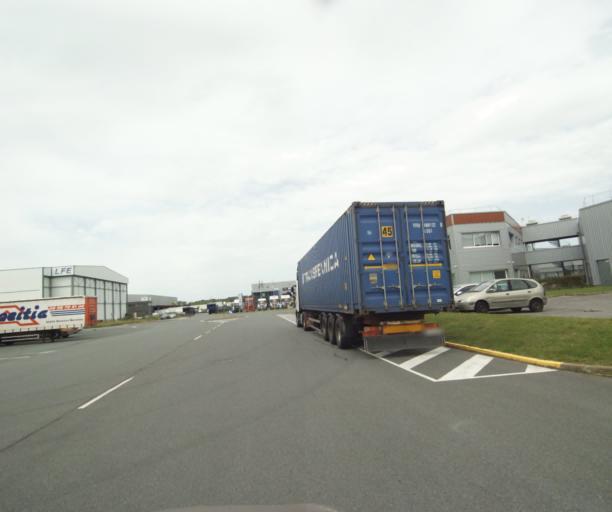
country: FR
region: Aquitaine
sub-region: Departement des Pyrenees-Atlantiques
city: Mouguerre
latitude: 43.4874
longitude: -1.4263
